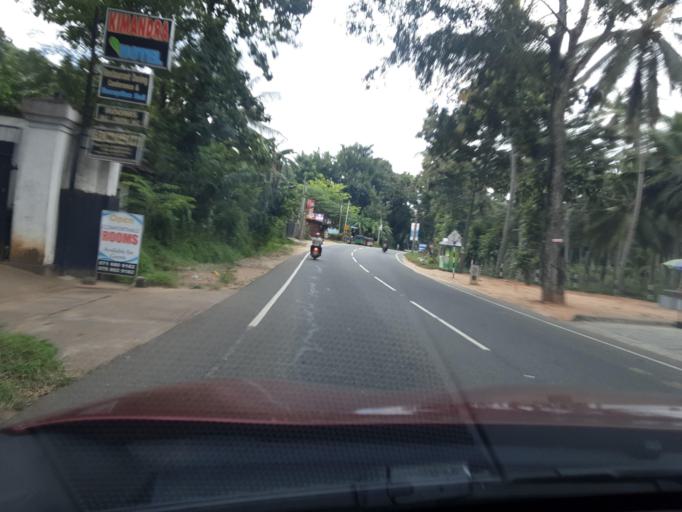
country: LK
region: North Western
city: Kurunegala
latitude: 7.4401
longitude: 80.2065
